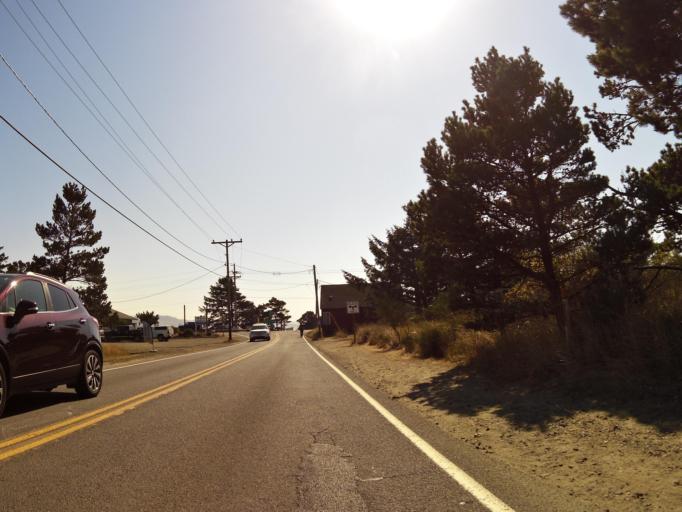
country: US
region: Oregon
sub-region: Tillamook County
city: Pacific City
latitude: 45.2030
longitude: -123.9660
